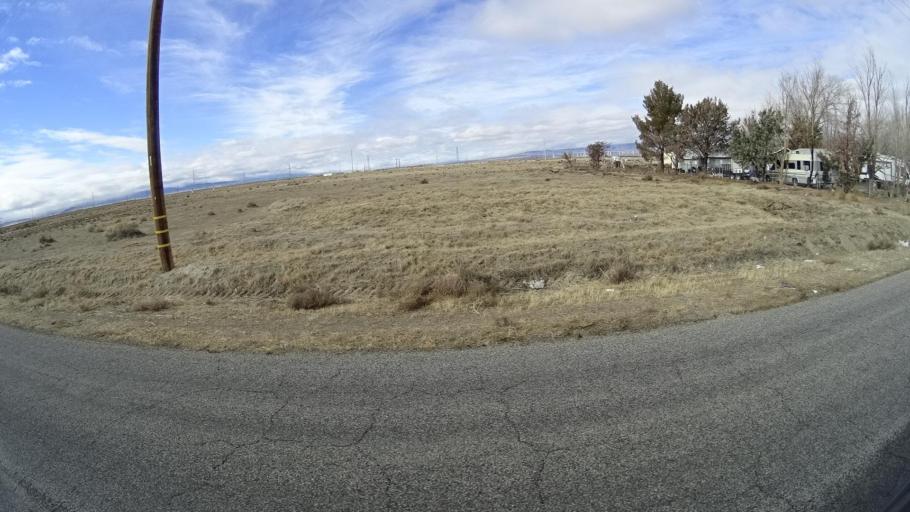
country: US
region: California
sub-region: Kern County
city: Rosamond
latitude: 34.8514
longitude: -118.3089
